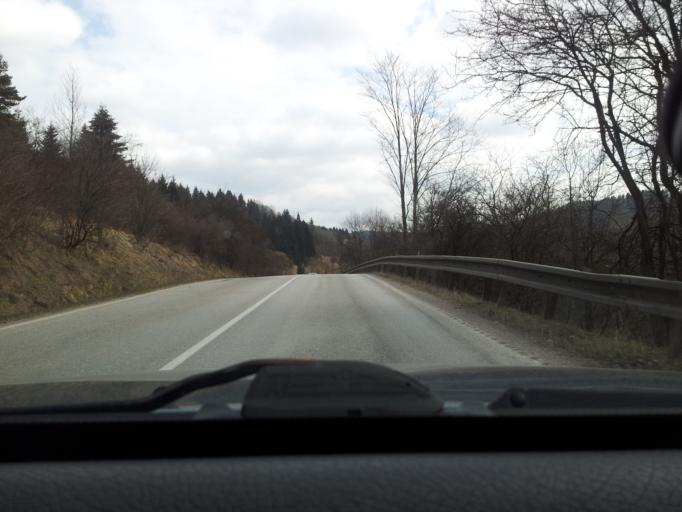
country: SK
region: Banskobystricky
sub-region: Okres Ziar nad Hronom
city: Kremnica
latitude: 48.7718
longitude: 18.8998
